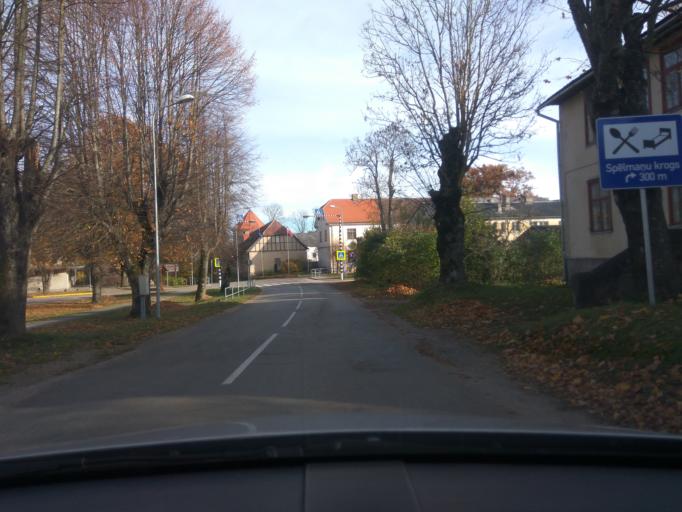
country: LV
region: Alsunga
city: Alsunga
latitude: 56.9817
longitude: 21.5654
